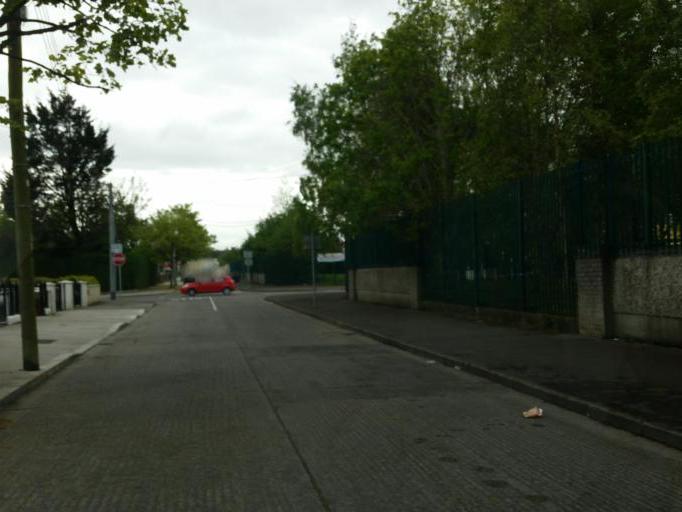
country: IE
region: Leinster
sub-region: Dublin City
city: Finglas
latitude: 53.3961
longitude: -6.3085
